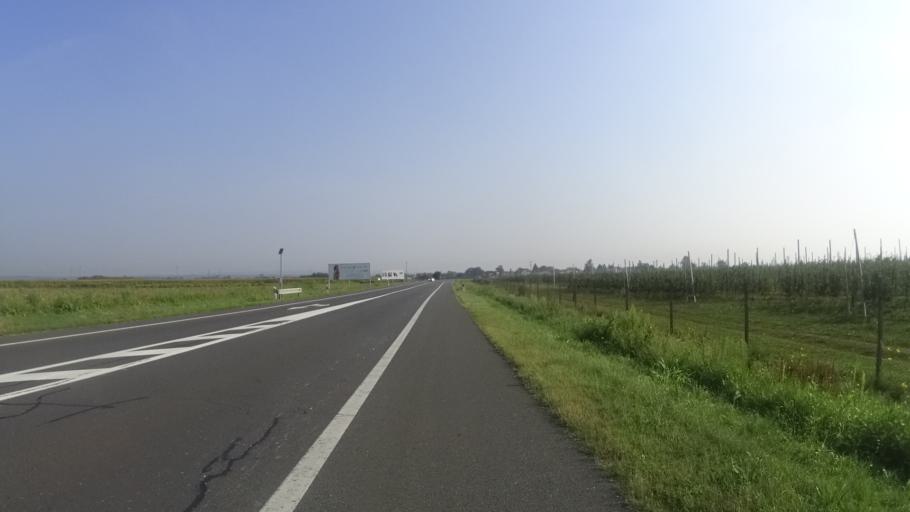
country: HR
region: Medimurska
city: Nedelisce
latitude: 46.3634
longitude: 16.3696
